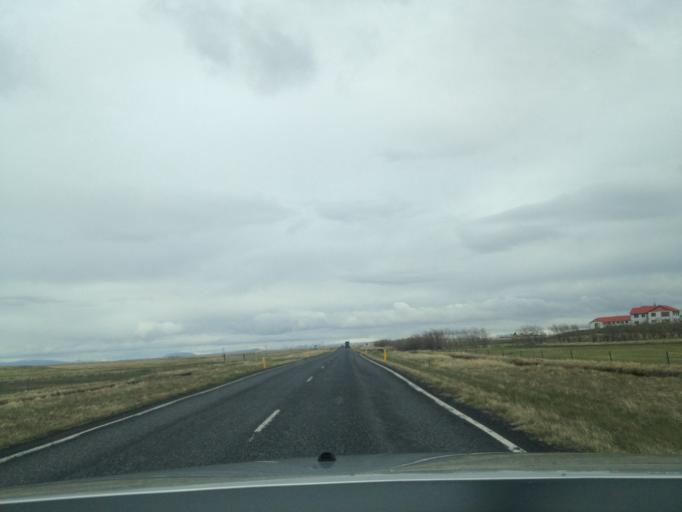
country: IS
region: South
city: Vestmannaeyjar
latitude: 63.7102
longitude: -20.2230
